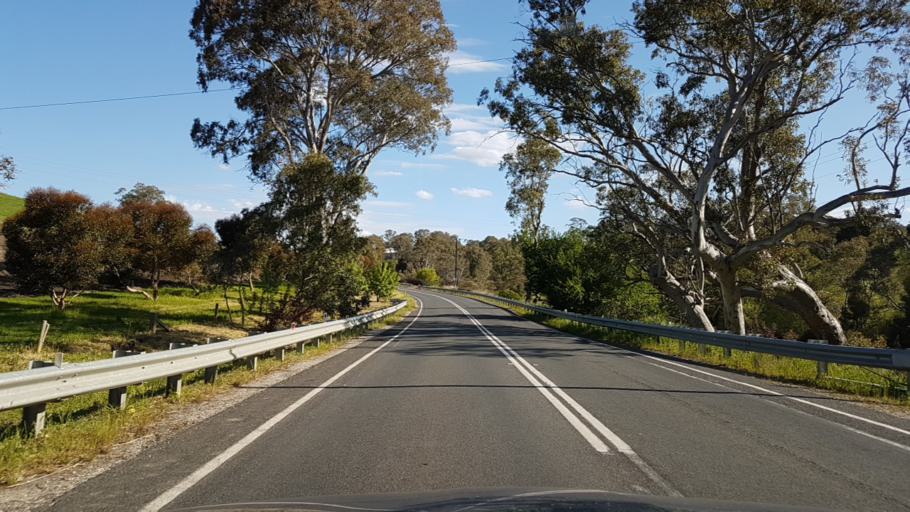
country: AU
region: South Australia
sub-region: Adelaide Hills
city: Gumeracha
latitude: -34.8447
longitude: 138.8929
